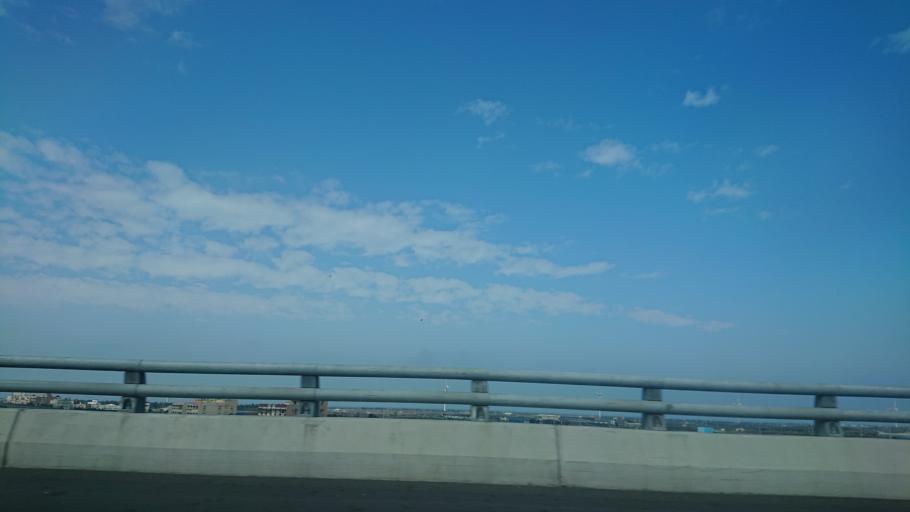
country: TW
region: Taiwan
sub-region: Changhua
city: Chang-hua
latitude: 23.9672
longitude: 120.3390
